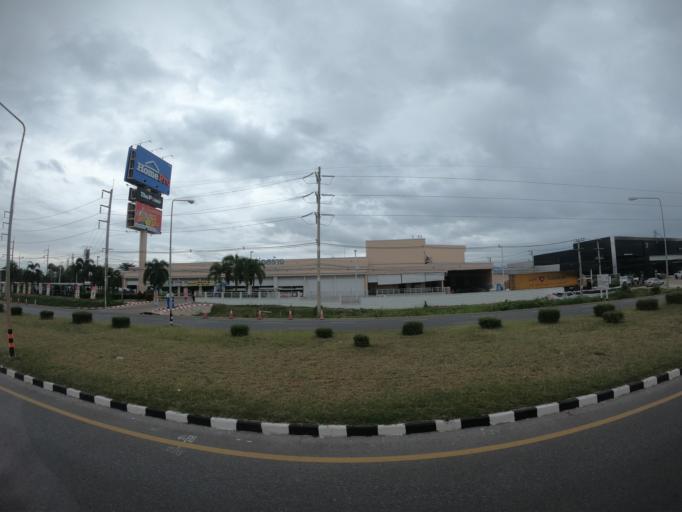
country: TH
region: Roi Et
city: Roi Et
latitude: 16.0615
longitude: 103.6191
